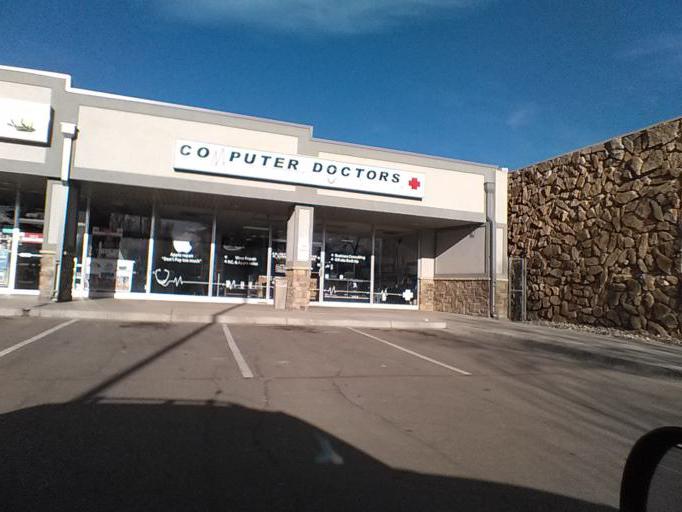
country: US
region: Colorado
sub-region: Larimer County
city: Fort Collins
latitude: 40.5656
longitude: -105.0774
